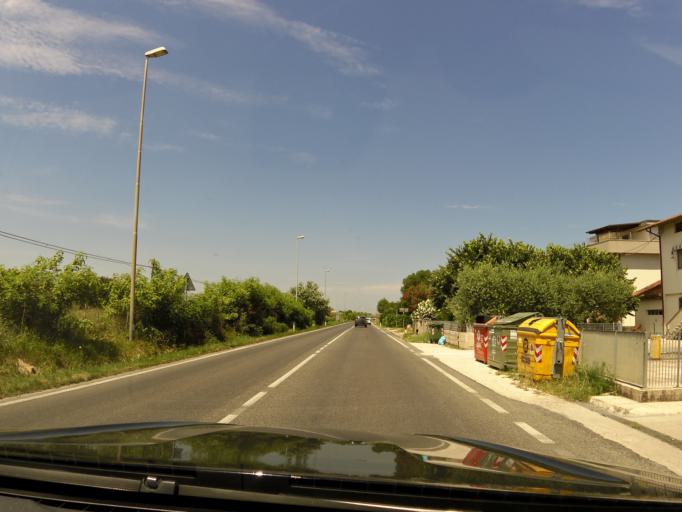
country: IT
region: The Marches
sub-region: Provincia di Pesaro e Urbino
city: Marotta
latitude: 43.7914
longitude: 13.1037
